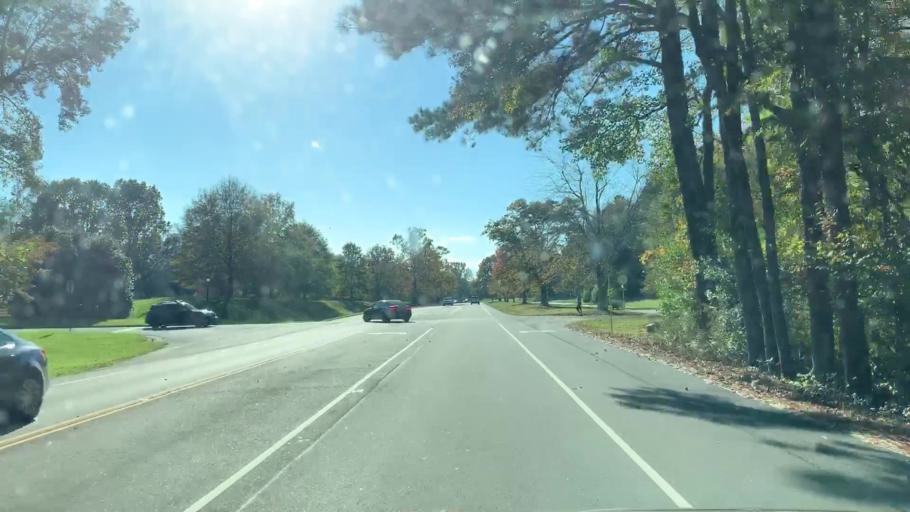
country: US
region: Virginia
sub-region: James City County
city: Williamsburg
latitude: 37.2348
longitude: -76.7732
